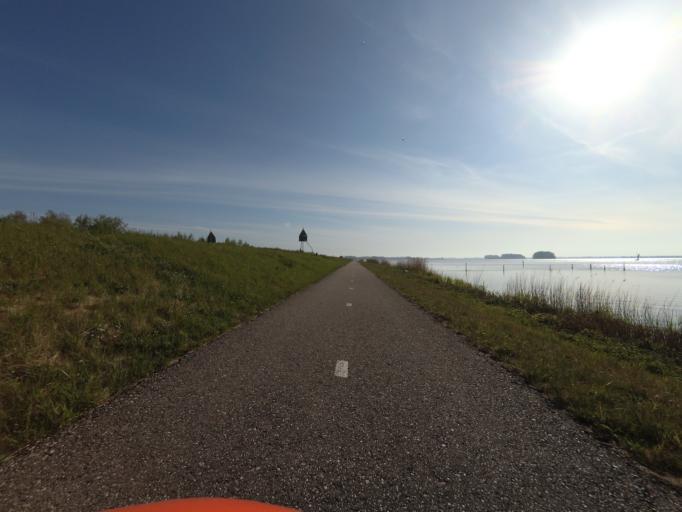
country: NL
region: Flevoland
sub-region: Gemeente Dronten
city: Biddinghuizen
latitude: 52.4088
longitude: 5.6970
